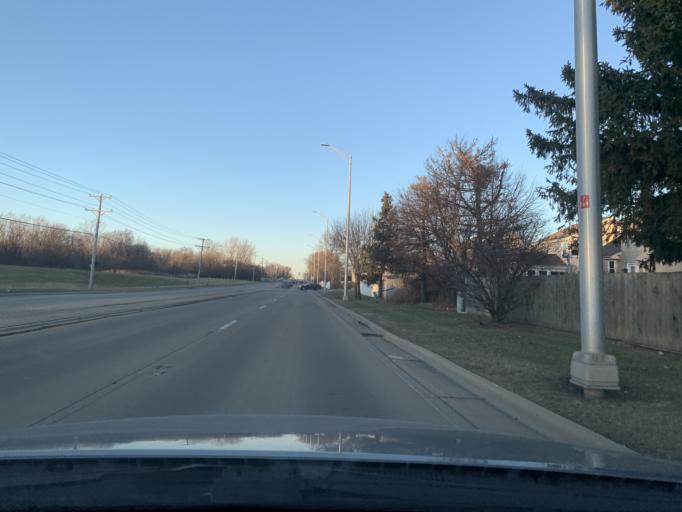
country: US
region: Illinois
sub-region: DuPage County
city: Roselle
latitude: 42.0103
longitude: -88.0604
